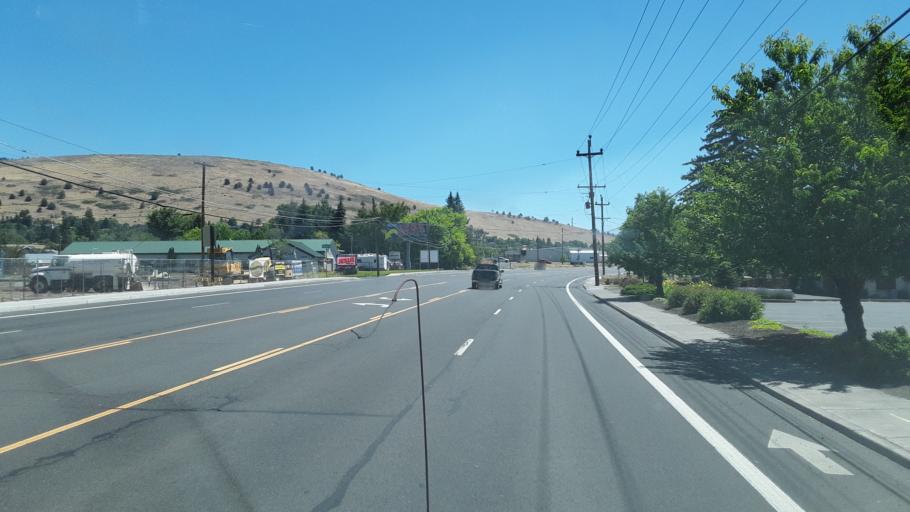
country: US
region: Oregon
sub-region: Klamath County
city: Altamont
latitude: 42.2064
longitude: -121.7161
